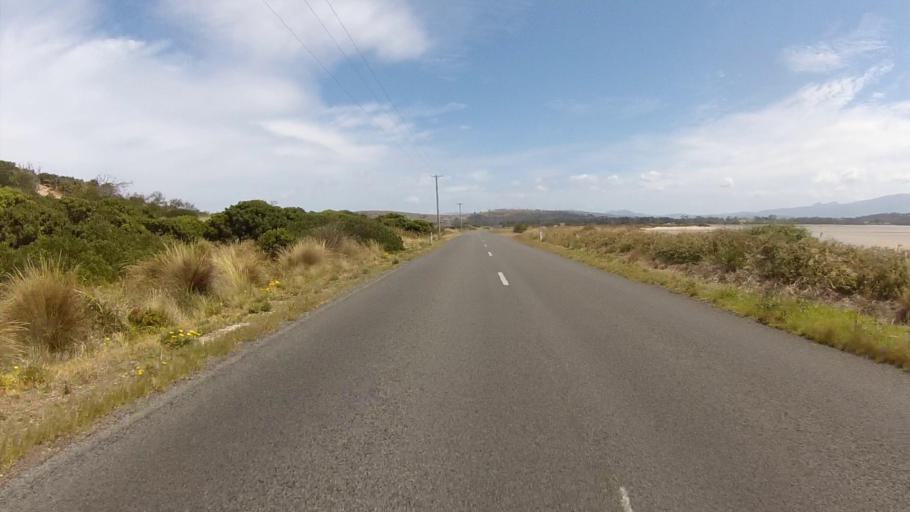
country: AU
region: Tasmania
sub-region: Clarence
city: Sandford
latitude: -43.0326
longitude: 147.4532
